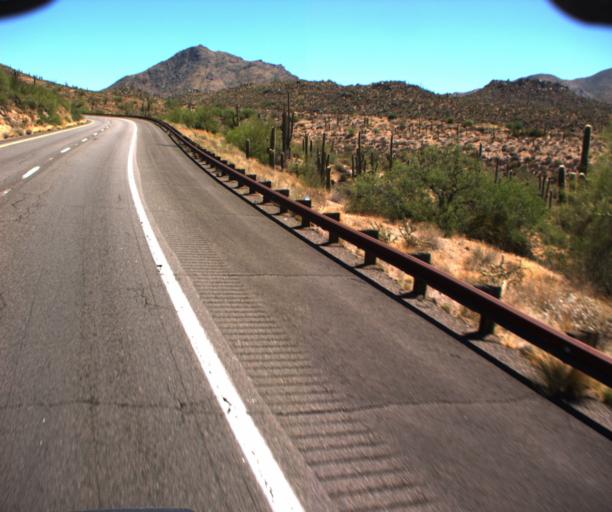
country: US
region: Arizona
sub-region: Gila County
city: Tonto Basin
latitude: 33.8108
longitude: -111.4878
